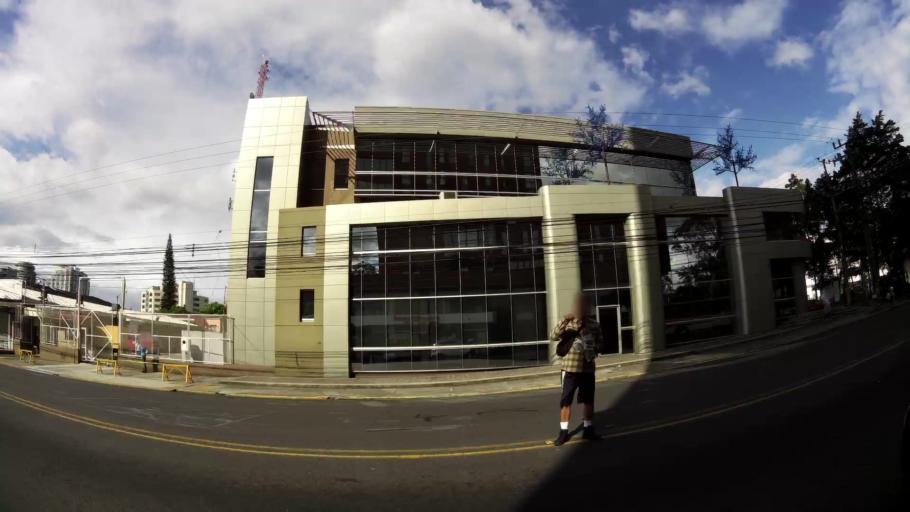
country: CR
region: San Jose
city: San Jose
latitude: 9.9357
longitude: -84.1101
